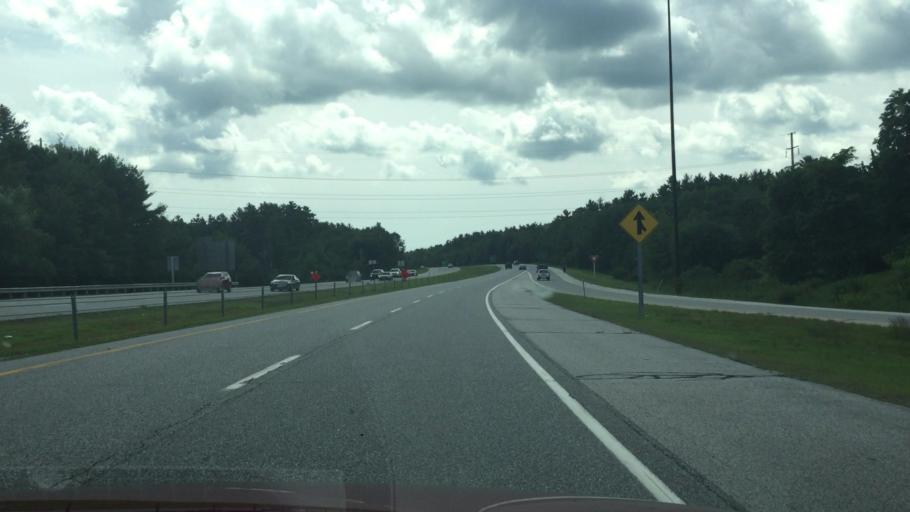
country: US
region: Maine
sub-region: York County
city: Saco
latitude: 43.5207
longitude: -70.4435
